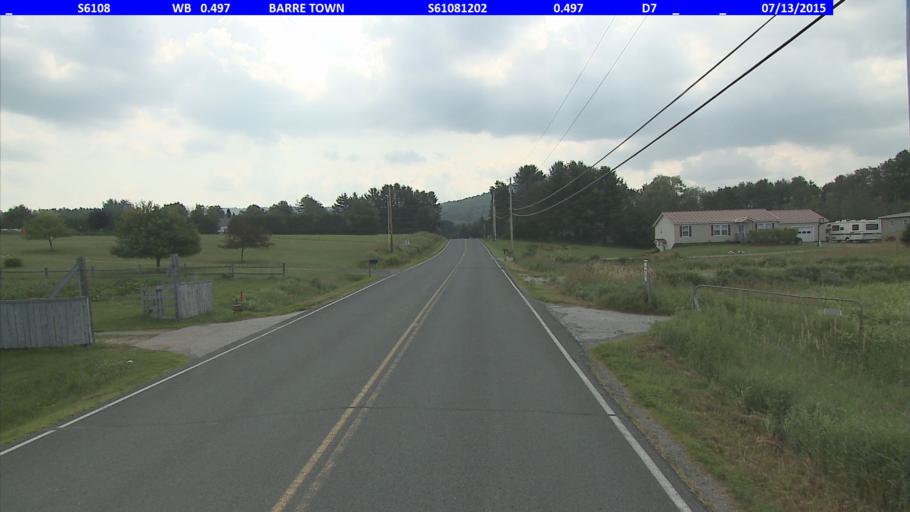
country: US
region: Vermont
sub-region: Washington County
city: Barre
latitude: 44.1858
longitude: -72.4756
